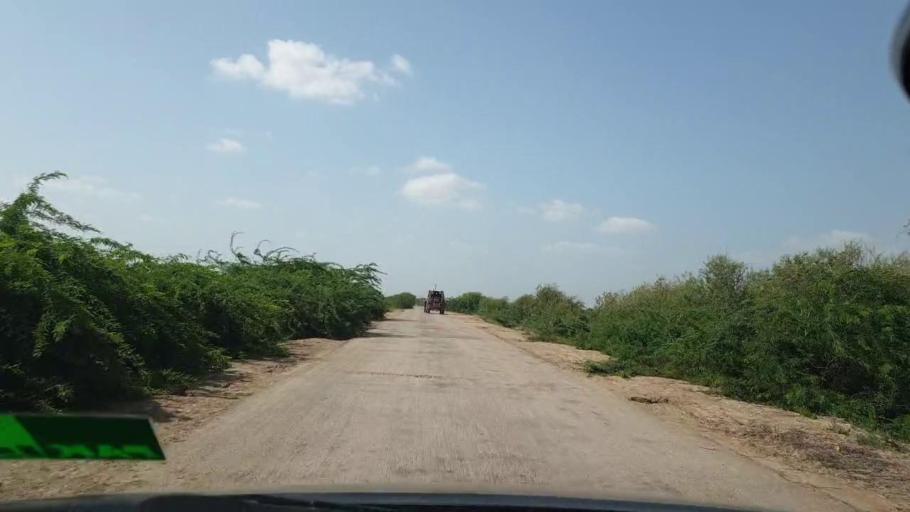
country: PK
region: Sindh
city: Tando Bago
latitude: 24.6664
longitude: 69.1972
